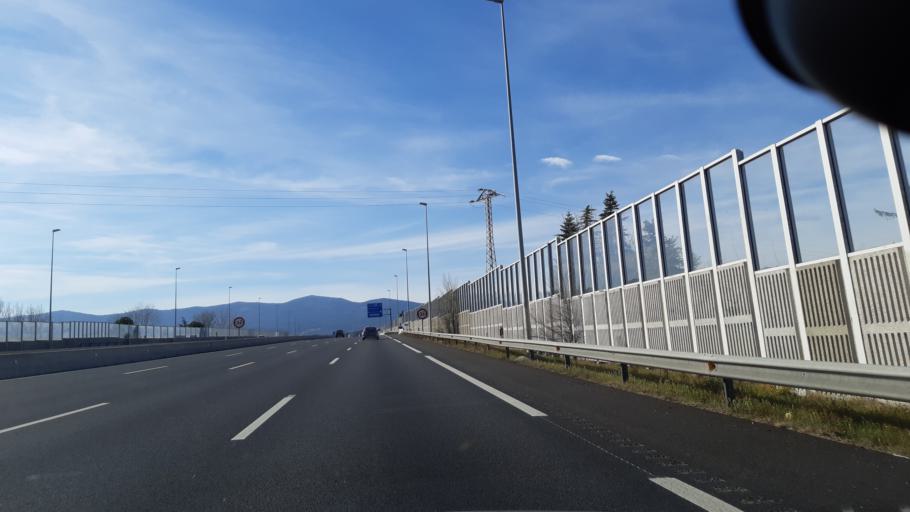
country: ES
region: Madrid
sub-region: Provincia de Madrid
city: Collado-Villalba
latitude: 40.6395
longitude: -4.0197
